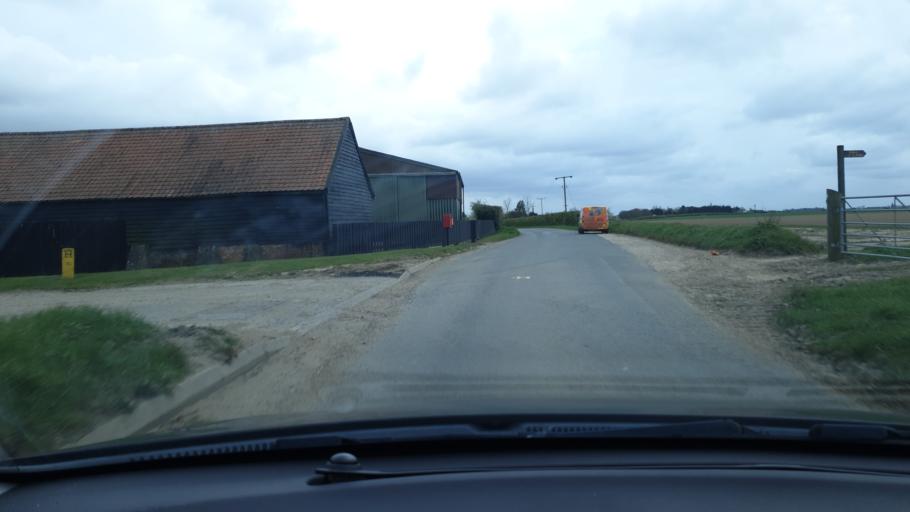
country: GB
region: England
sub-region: Essex
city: Mistley
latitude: 51.9251
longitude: 1.1776
